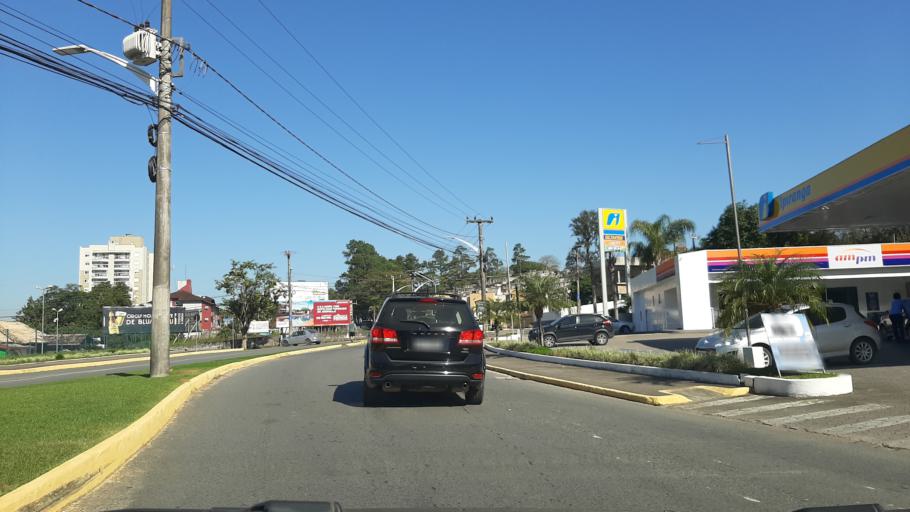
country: BR
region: Santa Catarina
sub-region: Joinville
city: Joinville
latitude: -26.3106
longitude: -48.8551
